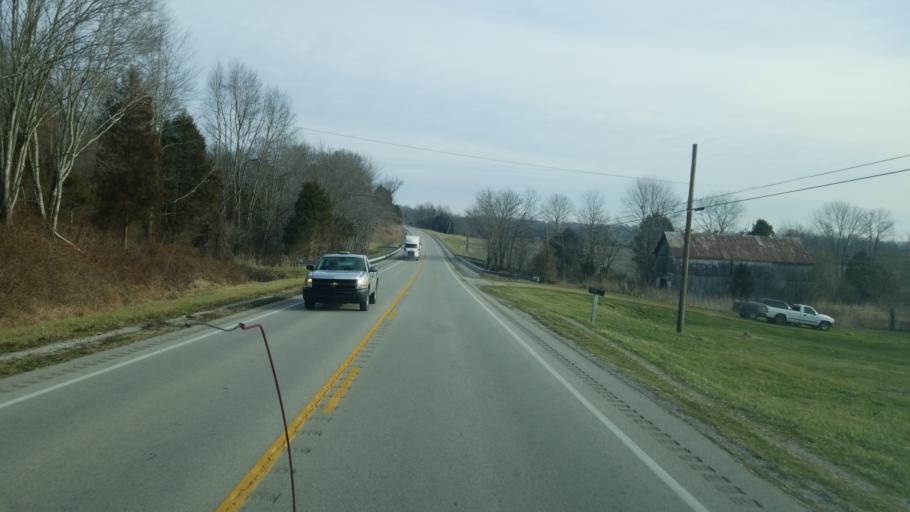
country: US
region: Kentucky
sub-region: Casey County
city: Liberty
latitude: 37.3481
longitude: -84.8782
